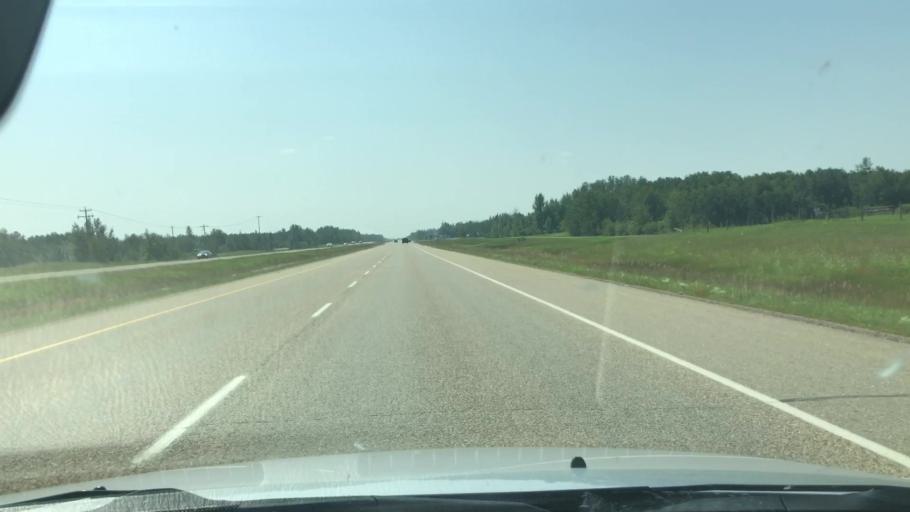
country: CA
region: Alberta
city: Devon
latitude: 53.4304
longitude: -113.7632
